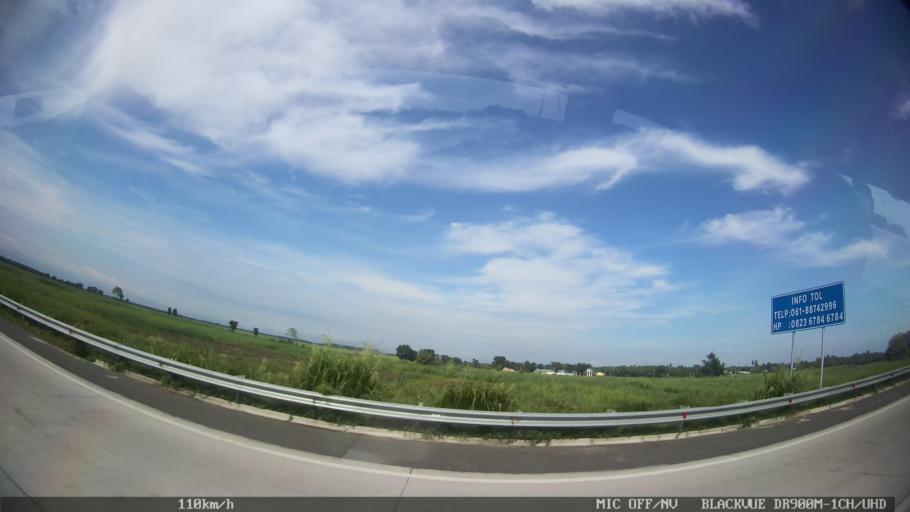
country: ID
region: North Sumatra
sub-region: Kabupaten Langkat
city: Stabat
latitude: 3.6985
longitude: 98.5400
